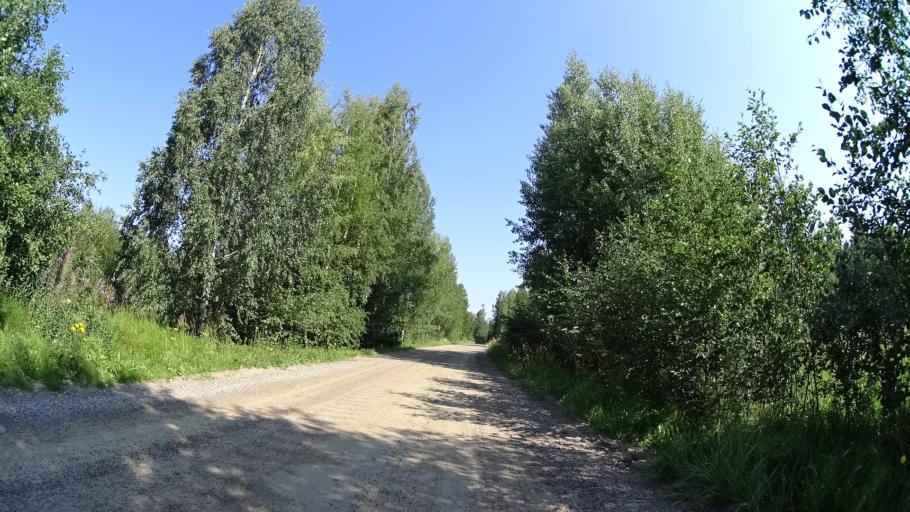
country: FI
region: Uusimaa
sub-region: Helsinki
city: Kerava
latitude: 60.3632
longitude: 25.1237
